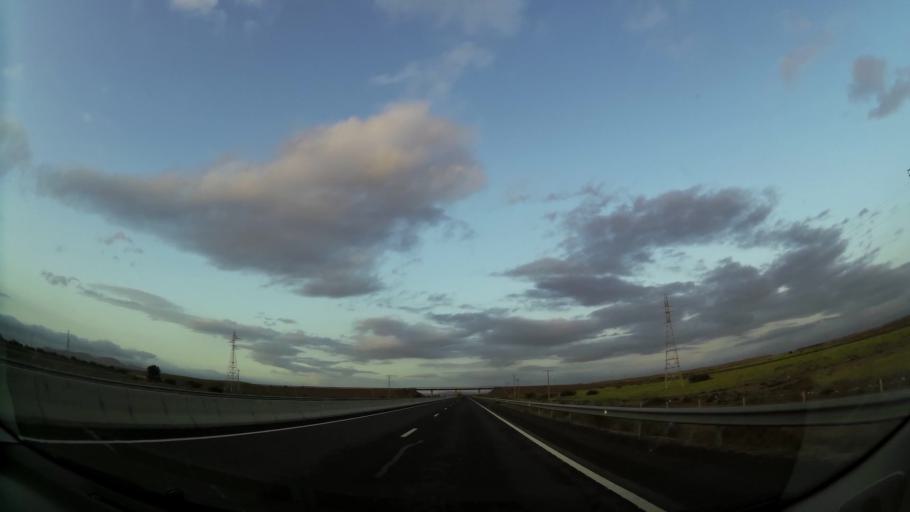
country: MA
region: Oriental
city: Taourirt
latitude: 34.5501
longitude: -2.8645
